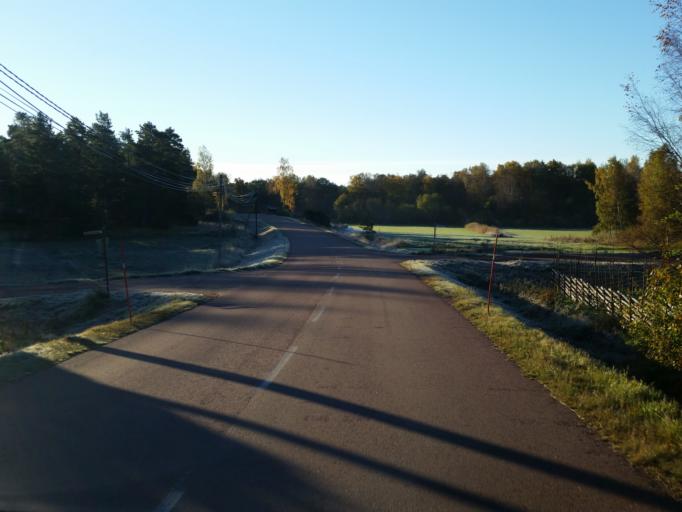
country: AX
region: Alands skaergard
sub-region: Vardoe
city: Vardoe
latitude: 60.2488
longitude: 20.3712
